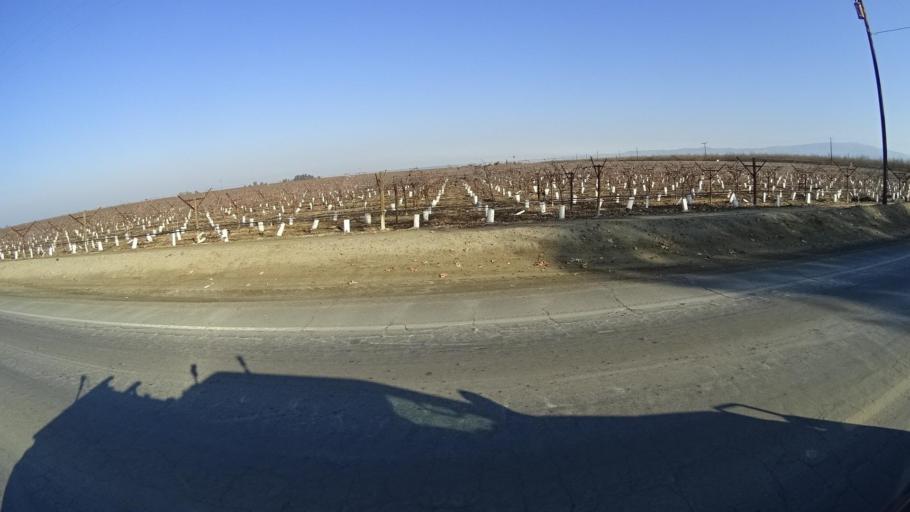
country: US
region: California
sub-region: Kern County
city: Lamont
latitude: 35.2524
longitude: -118.9339
